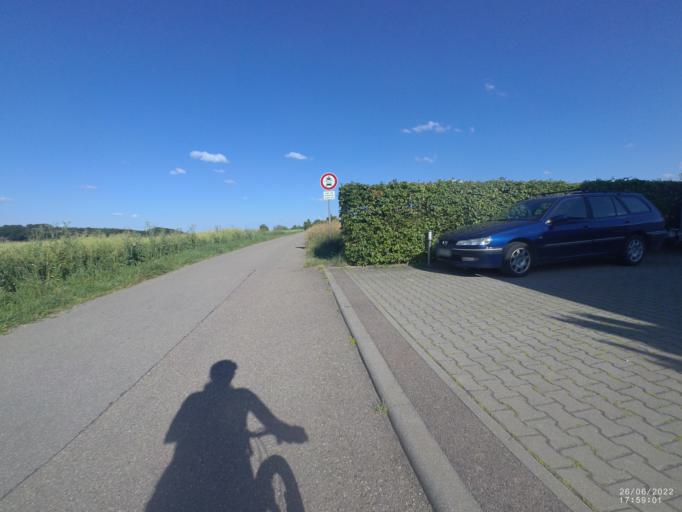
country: DE
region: Baden-Wuerttemberg
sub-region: Regierungsbezirk Stuttgart
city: Bohmenkirch
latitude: 48.6416
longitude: 9.9659
